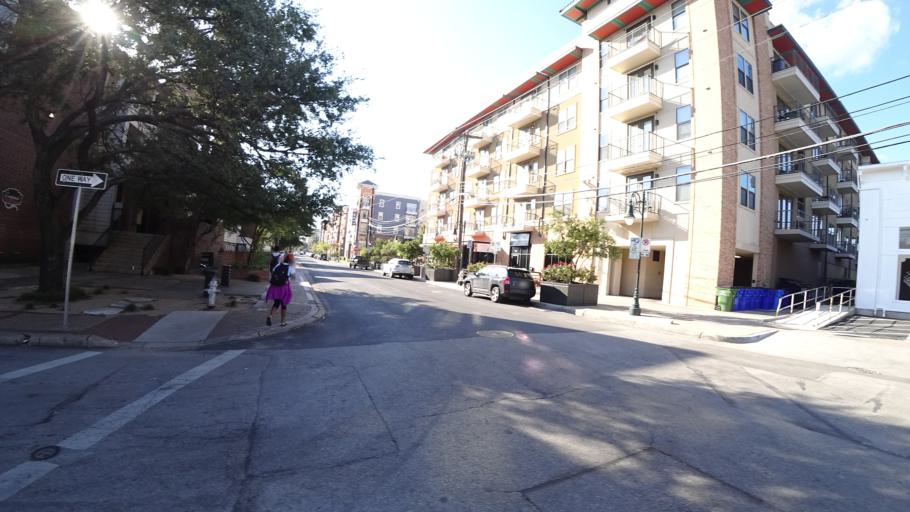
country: US
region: Texas
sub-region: Travis County
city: Austin
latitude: 30.2905
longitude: -97.7421
